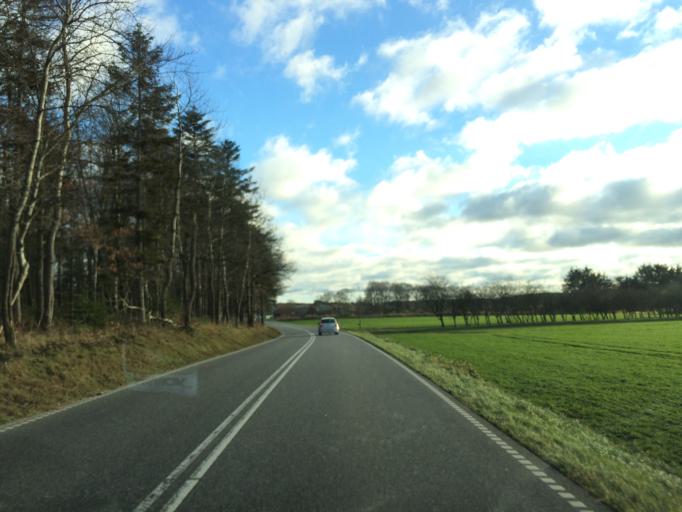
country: DK
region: Central Jutland
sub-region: Herning Kommune
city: Kibaek
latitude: 55.9270
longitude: 8.9013
